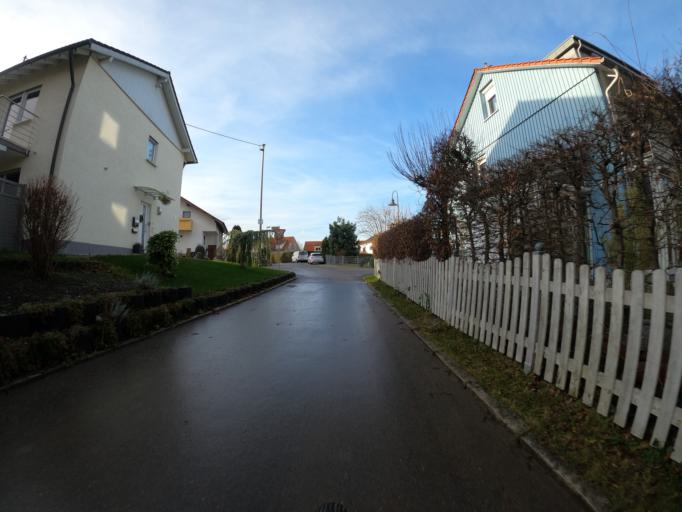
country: DE
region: Baden-Wuerttemberg
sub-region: Regierungsbezirk Stuttgart
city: Boll
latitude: 48.6461
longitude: 9.6214
